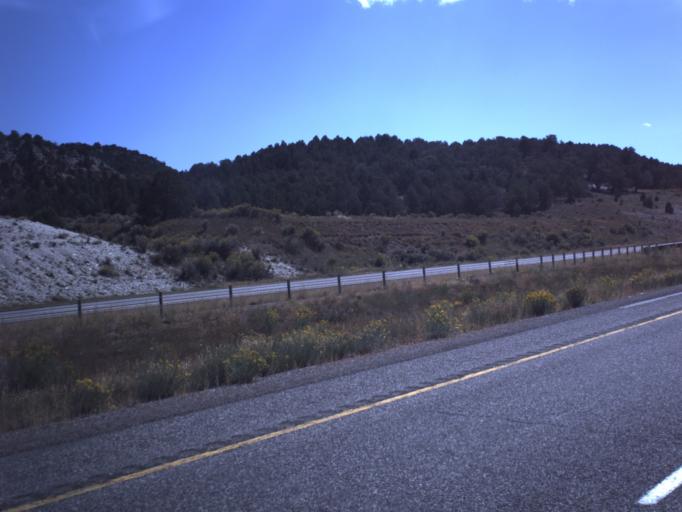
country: US
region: Utah
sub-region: Sevier County
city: Salina
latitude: 38.8696
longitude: -111.5529
